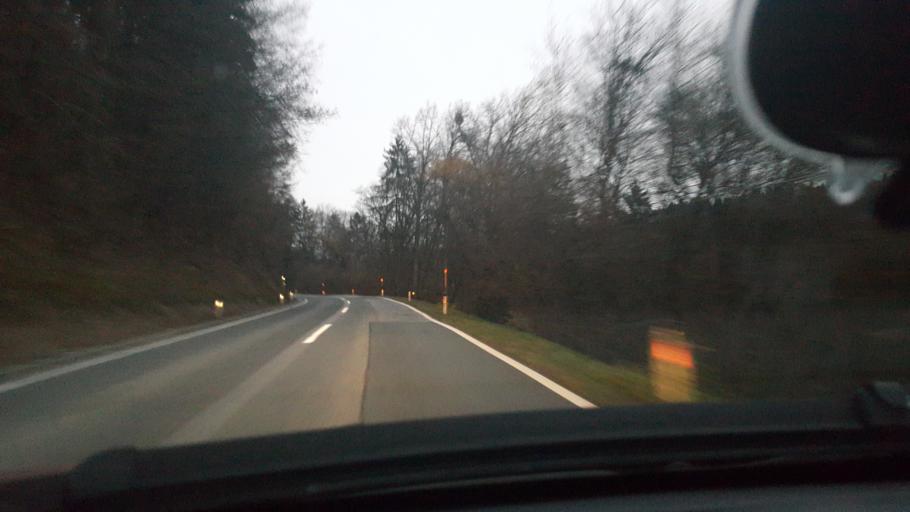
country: AT
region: Carinthia
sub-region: Politischer Bezirk Wolfsberg
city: Sankt Paul im Levanttal
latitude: 46.6667
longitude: 14.8593
